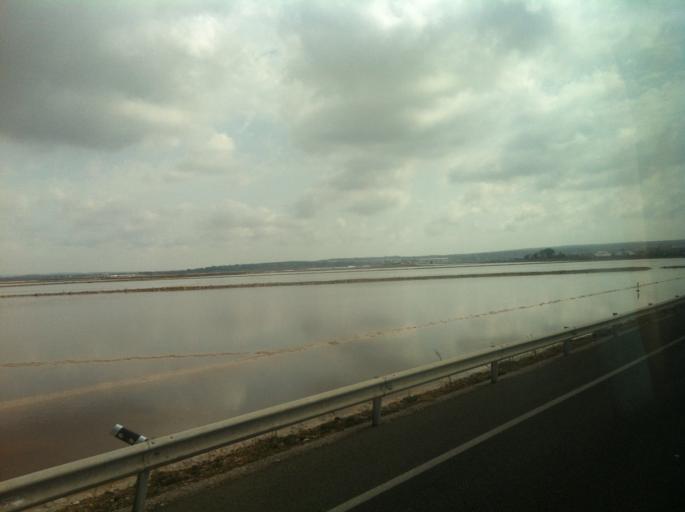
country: ES
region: Valencia
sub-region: Provincia de Alicante
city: Santa Pola
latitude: 38.1852
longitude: -0.6081
